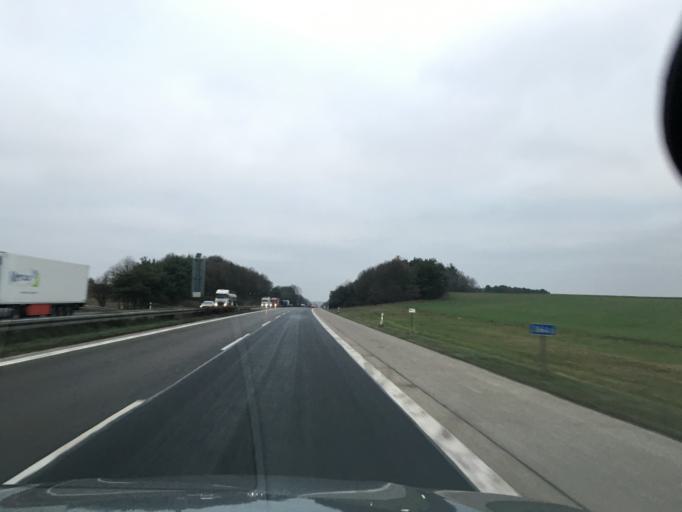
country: DE
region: Bavaria
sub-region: Regierungsbezirk Mittelfranken
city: Grossenseebach
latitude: 49.6743
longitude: 10.8726
